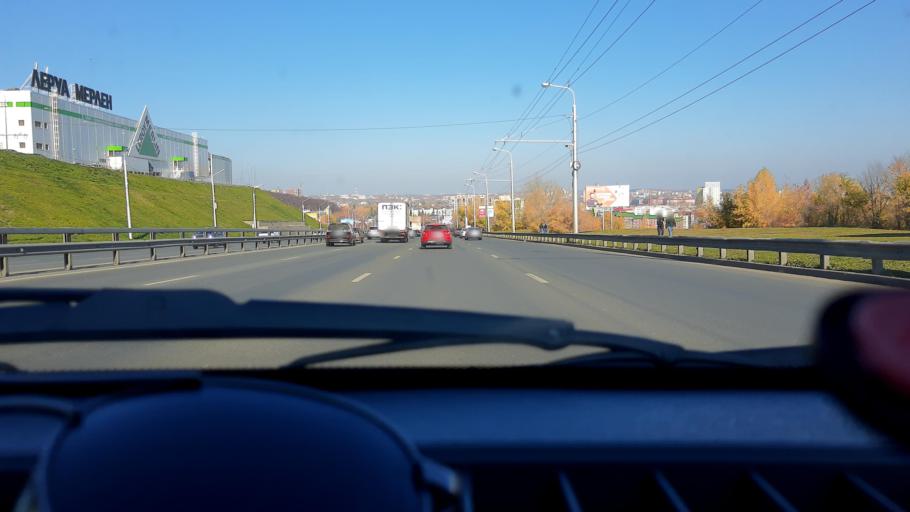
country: RU
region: Bashkortostan
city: Ufa
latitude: 54.7578
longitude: 56.0393
